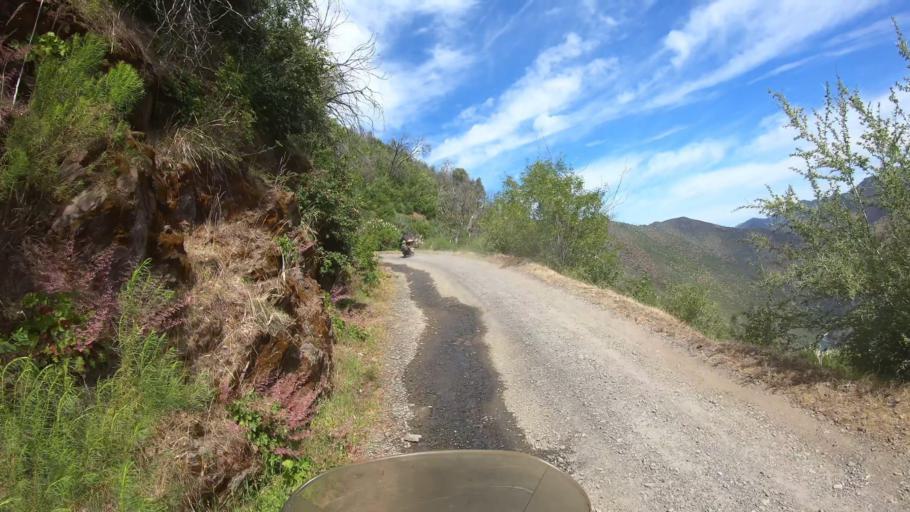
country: US
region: California
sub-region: Tuolumne County
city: Tuolumne City
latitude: 37.8319
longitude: -120.0993
